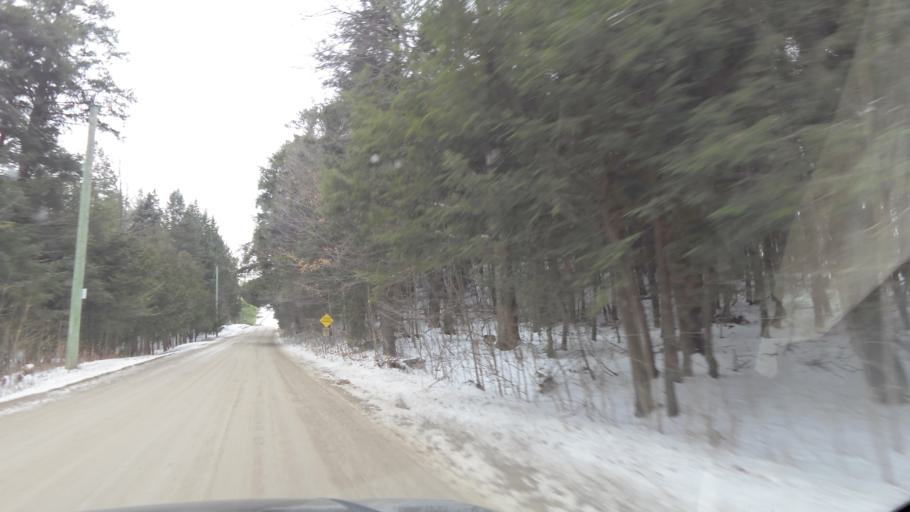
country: CA
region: Ontario
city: Vaughan
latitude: 43.9210
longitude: -79.6053
